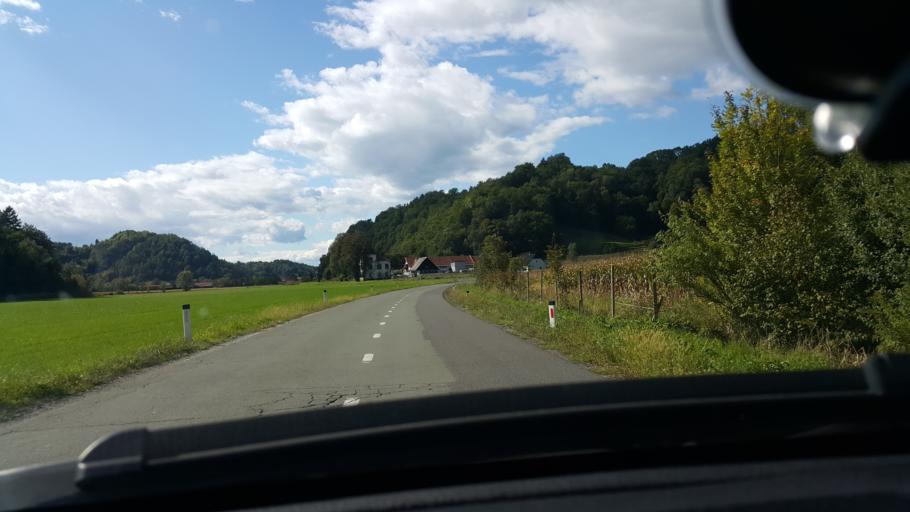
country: SI
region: Kungota
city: Zgornja Kungota
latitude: 46.6381
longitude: 15.6070
